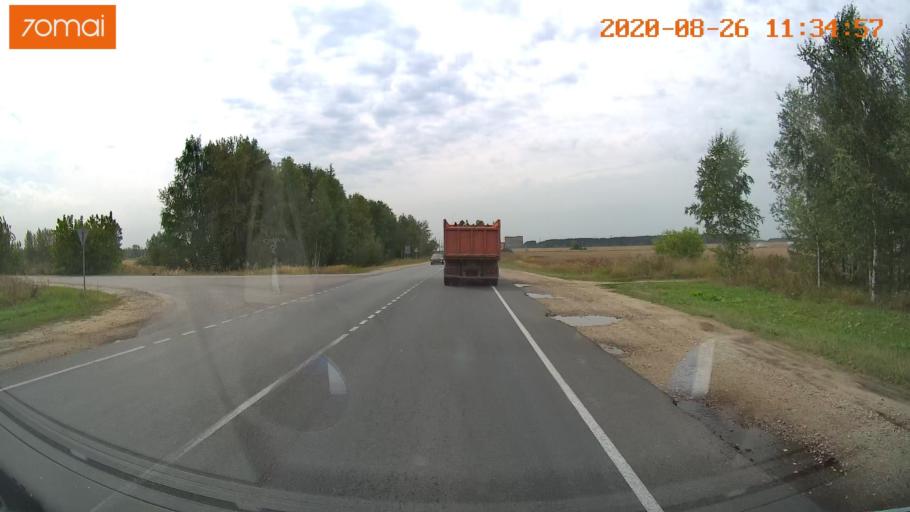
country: RU
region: Rjazan
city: Shilovo
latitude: 54.2794
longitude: 40.8383
